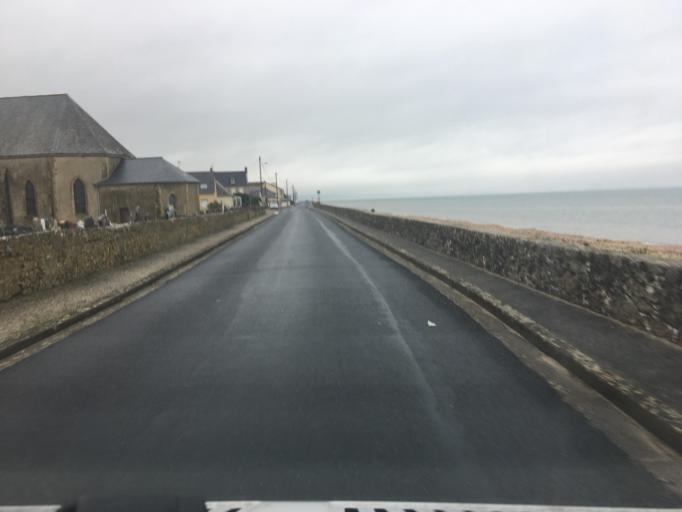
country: FR
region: Lower Normandy
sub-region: Departement de la Manche
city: Saint-Vaast-la-Hougue
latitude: 49.4948
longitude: -1.2655
